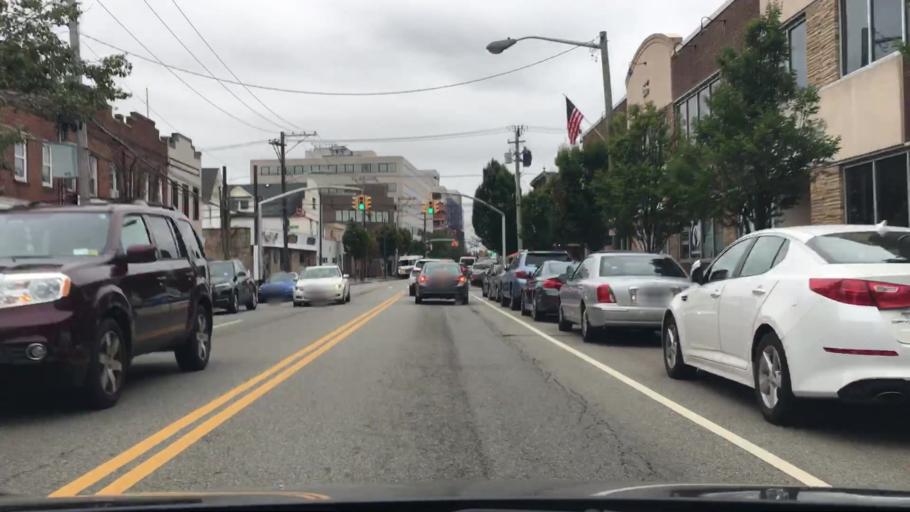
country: US
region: New York
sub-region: Nassau County
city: Mineola
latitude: 40.7436
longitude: -73.6413
